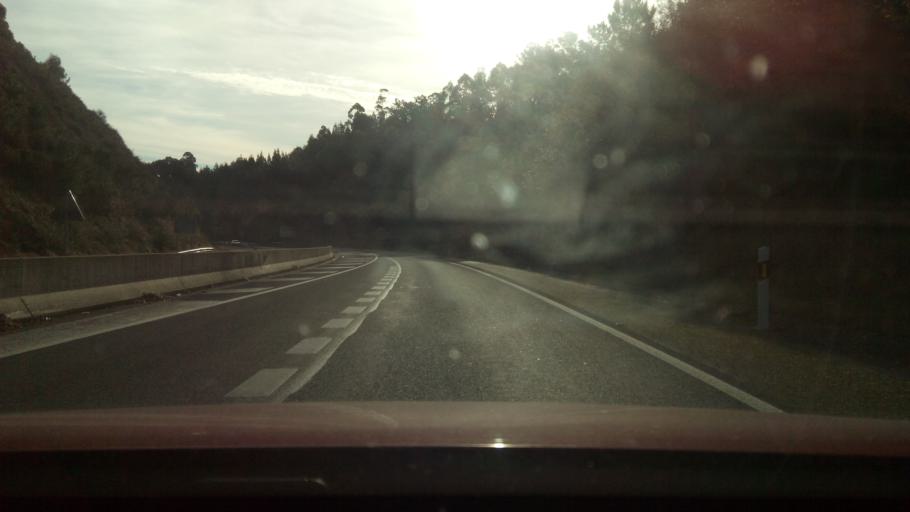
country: ES
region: Galicia
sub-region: Provincia de Pontevedra
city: Sanxenxo
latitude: 42.4198
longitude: -8.8362
